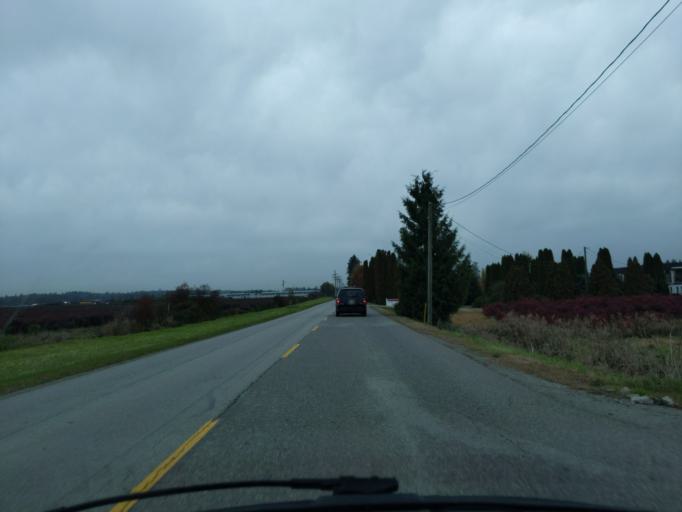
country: CA
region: British Columbia
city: Pitt Meadows
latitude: 49.2225
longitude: -122.7047
